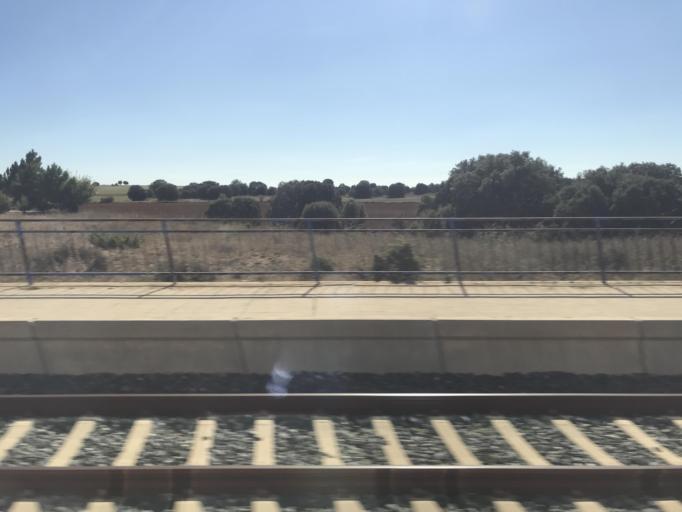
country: ES
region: Castille-La Mancha
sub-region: Provincia de Guadalajara
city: Alaminos
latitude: 40.8968
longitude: -2.7042
